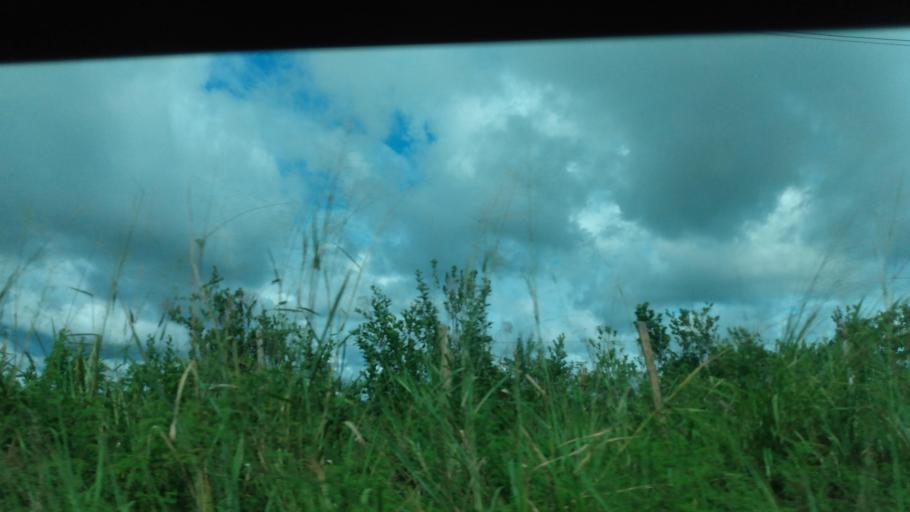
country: BR
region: Pernambuco
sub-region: Maraial
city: Maraial
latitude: -8.7879
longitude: -35.8794
